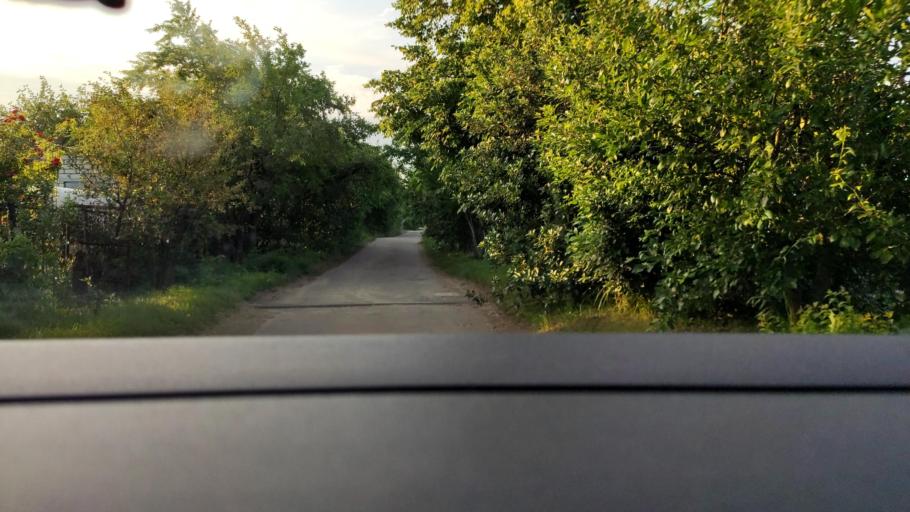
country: RU
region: Voronezj
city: Ramon'
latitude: 51.9094
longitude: 39.1769
